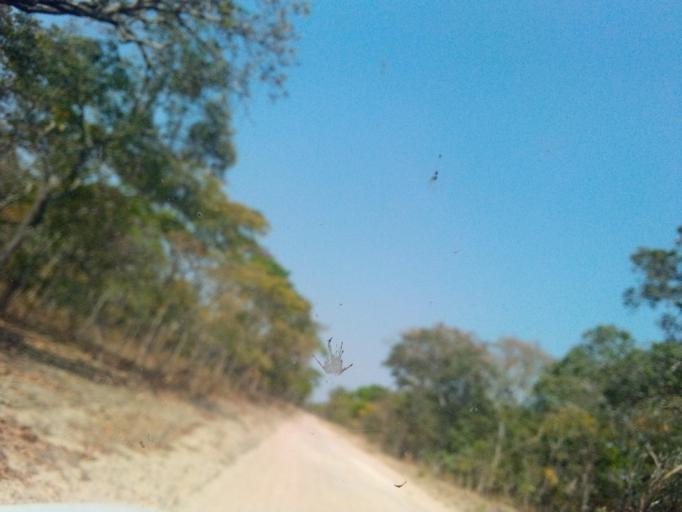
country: ZM
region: Northern
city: Mpika
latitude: -12.2259
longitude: 30.8933
